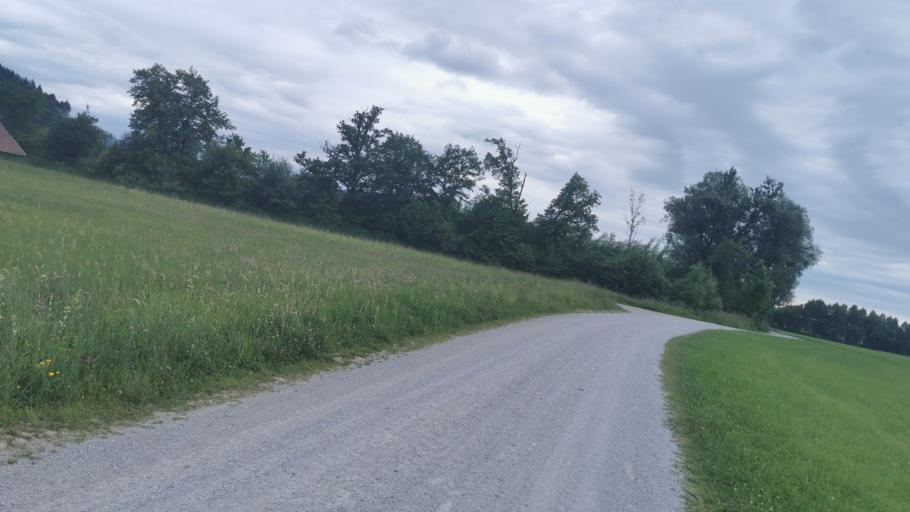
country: DE
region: Bavaria
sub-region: Upper Bavaria
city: Piding
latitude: 47.7628
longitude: 12.9688
